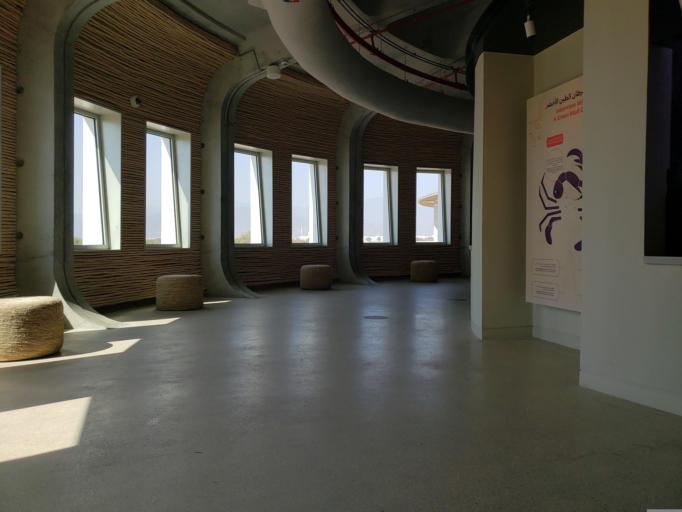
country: AE
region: Al Fujayrah
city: Al Fujayrah
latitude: 25.0130
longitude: 56.3616
